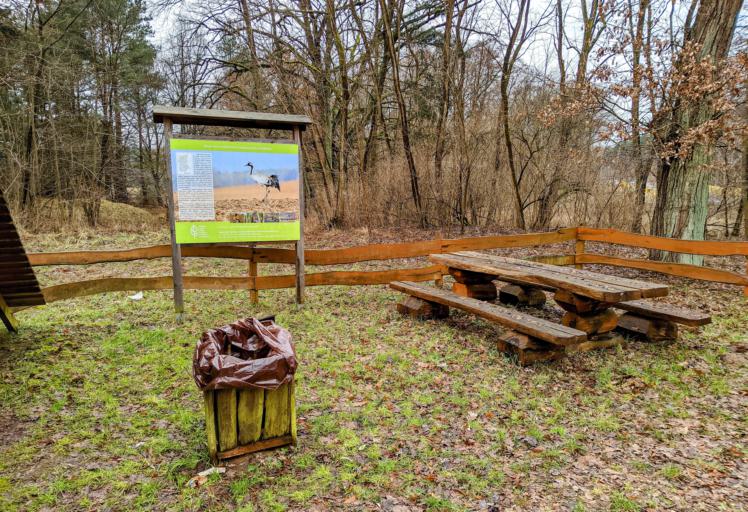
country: PL
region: Lubusz
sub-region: Powiat swiebodzinski
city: Miedzylesie
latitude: 52.1152
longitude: 15.4154
